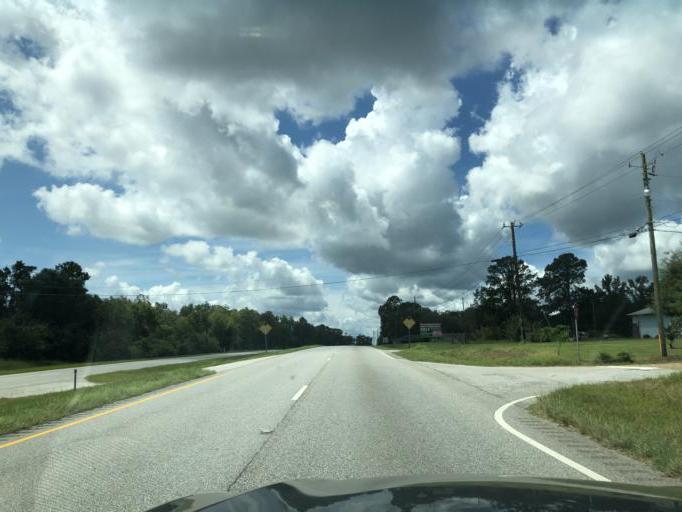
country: US
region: Alabama
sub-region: Barbour County
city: Eufaula
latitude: 31.9326
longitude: -85.1385
